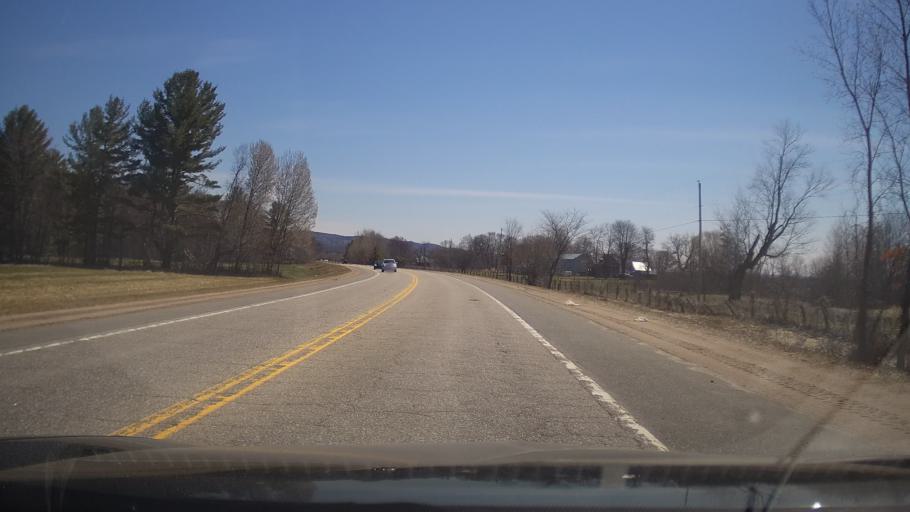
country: CA
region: Ontario
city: Arnprior
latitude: 45.5544
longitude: -76.1211
